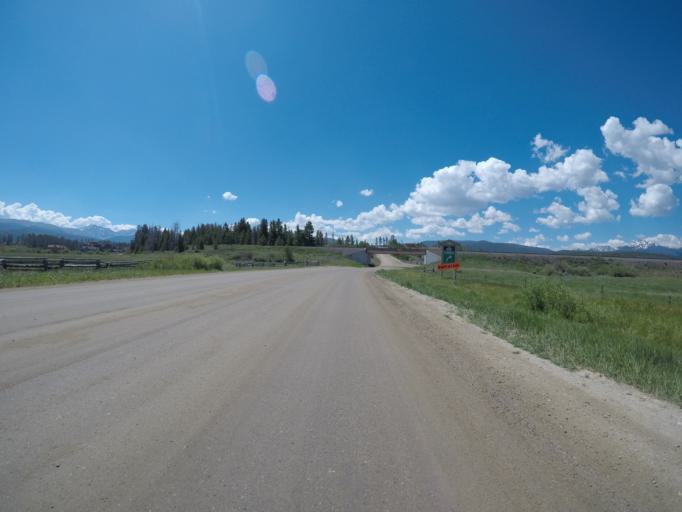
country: US
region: Colorado
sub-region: Grand County
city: Fraser
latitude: 39.9413
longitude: -105.8126
